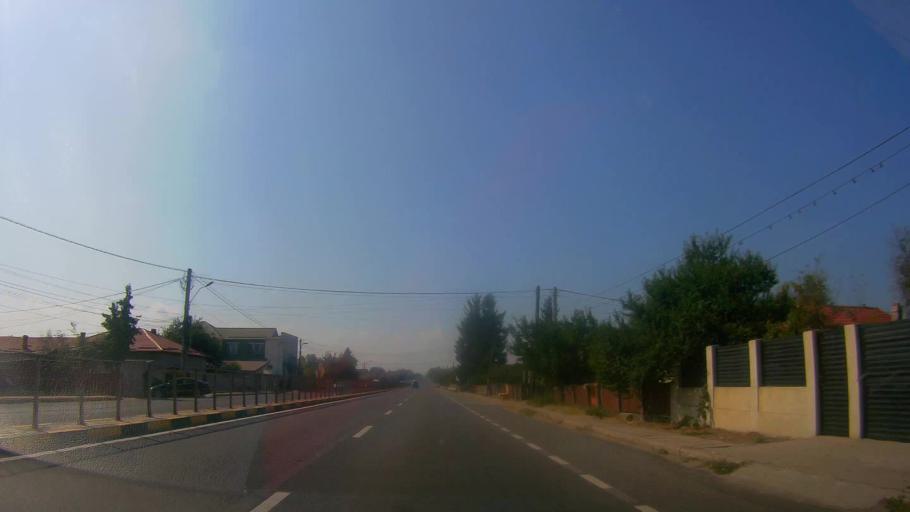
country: RO
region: Giurgiu
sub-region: Comuna Fratesti
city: Remus
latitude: 43.9416
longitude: 25.9785
